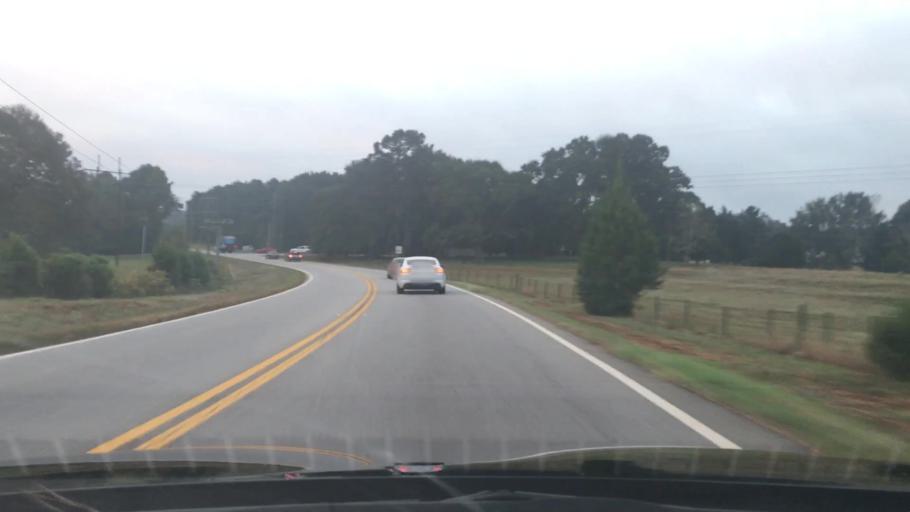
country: US
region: Georgia
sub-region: Fayette County
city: Peachtree City
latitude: 33.3746
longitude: -84.6679
